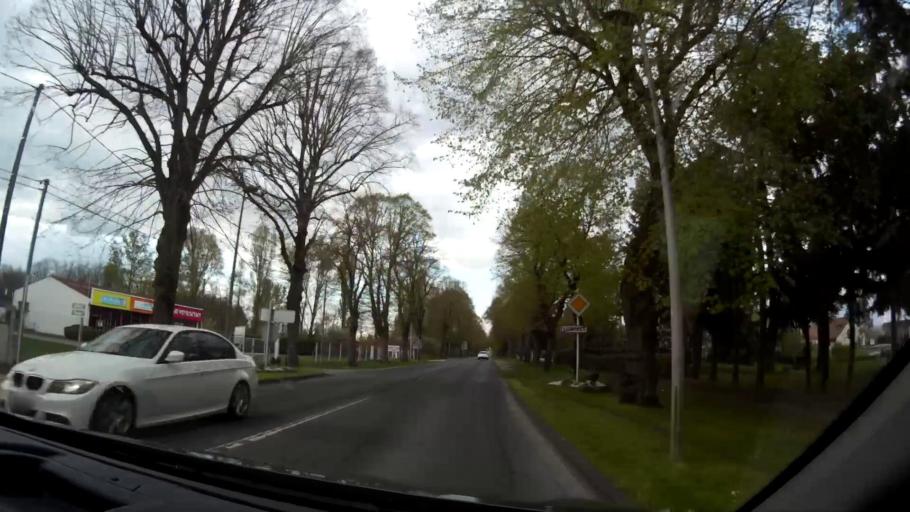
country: FR
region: Centre
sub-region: Departement du Loir-et-Cher
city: Contres
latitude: 47.4296
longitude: 1.4279
